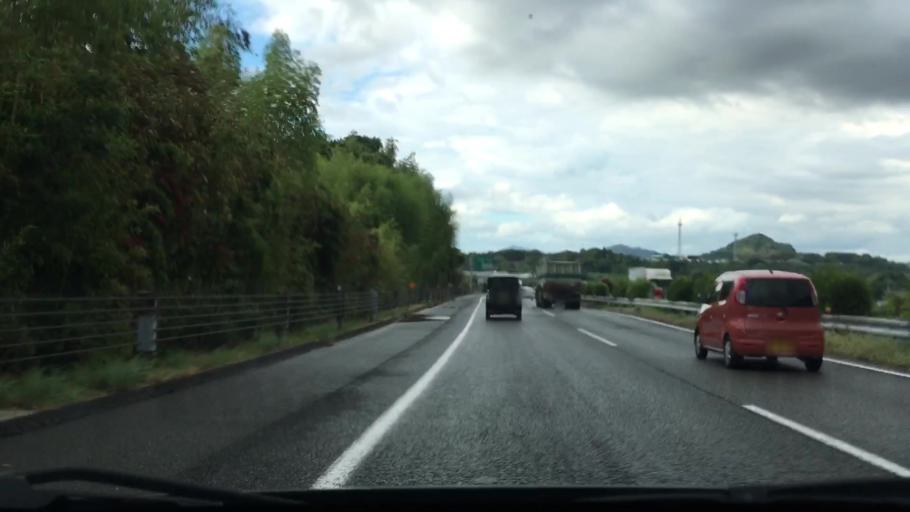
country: JP
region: Fukuoka
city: Koga
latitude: 33.7267
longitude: 130.5035
